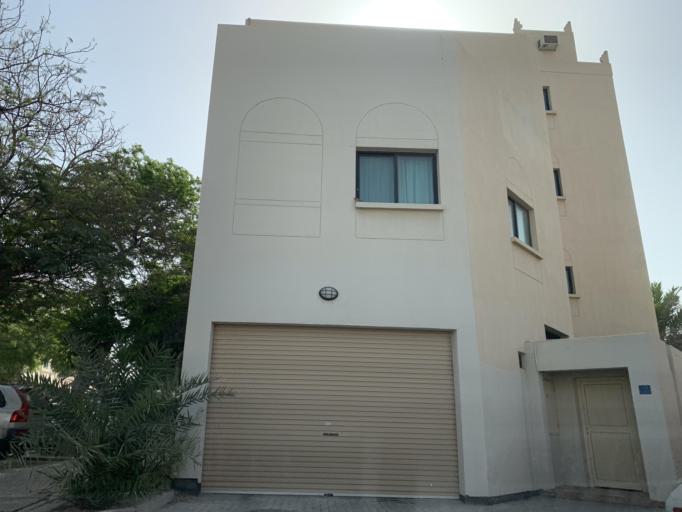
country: BH
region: Northern
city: Madinat `Isa
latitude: 26.1719
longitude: 50.5364
